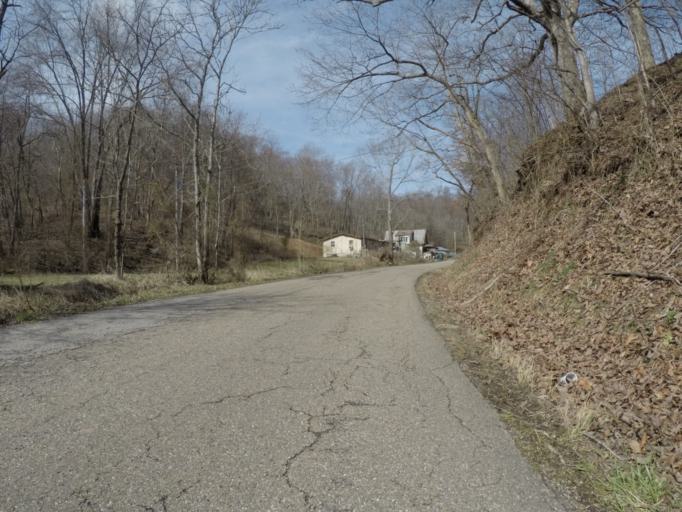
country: US
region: Ohio
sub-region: Lawrence County
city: Burlington
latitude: 38.4812
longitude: -82.5321
